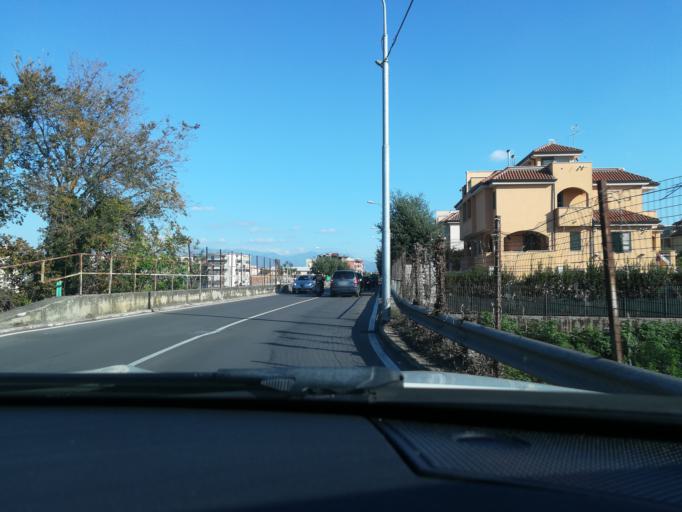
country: IT
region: Campania
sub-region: Provincia di Napoli
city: Sant'Anastasia
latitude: 40.8724
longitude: 14.3953
